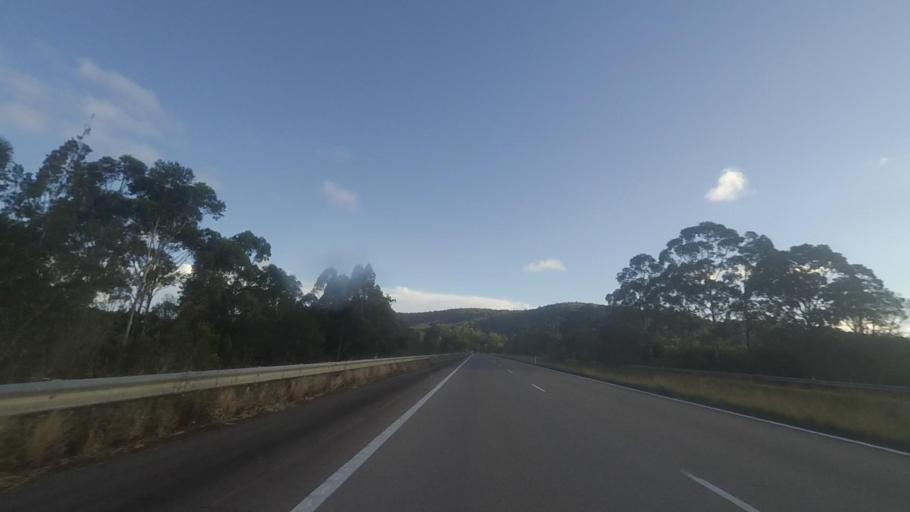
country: AU
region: New South Wales
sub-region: Great Lakes
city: Nabiac
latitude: -32.2674
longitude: 152.3283
